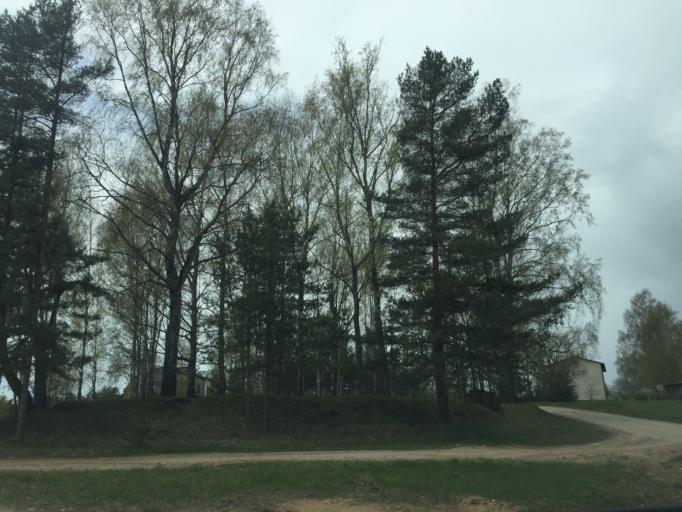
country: LV
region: Kekava
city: Kekava
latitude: 56.7631
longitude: 24.2939
